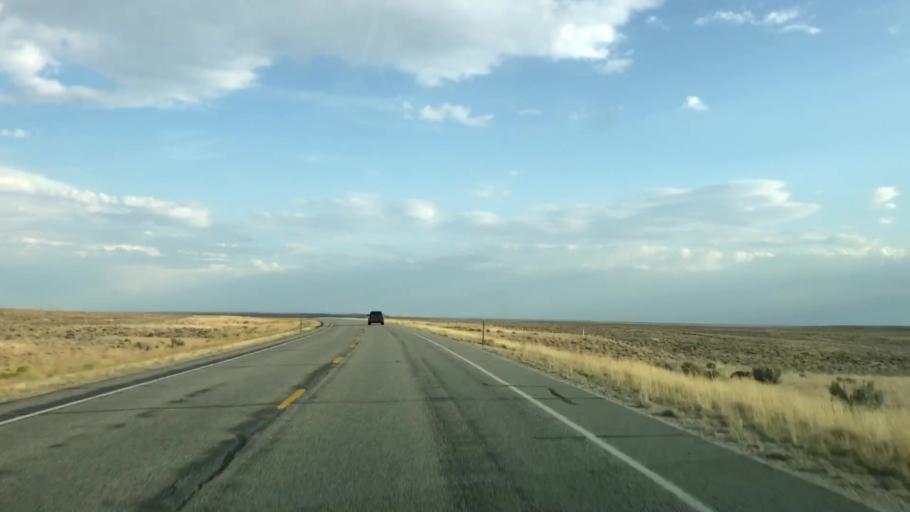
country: US
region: Wyoming
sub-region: Sublette County
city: Marbleton
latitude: 42.3384
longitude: -109.5211
